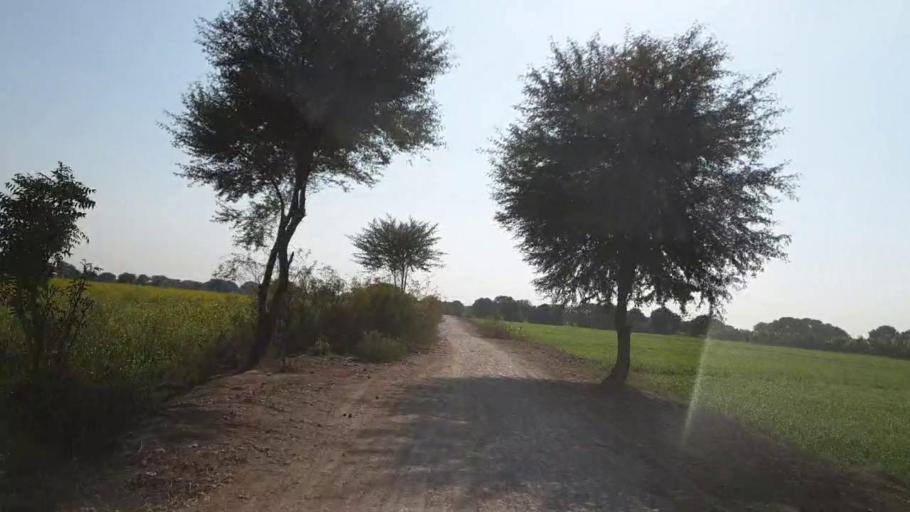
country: PK
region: Sindh
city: Tando Jam
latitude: 25.5016
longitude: 68.5006
